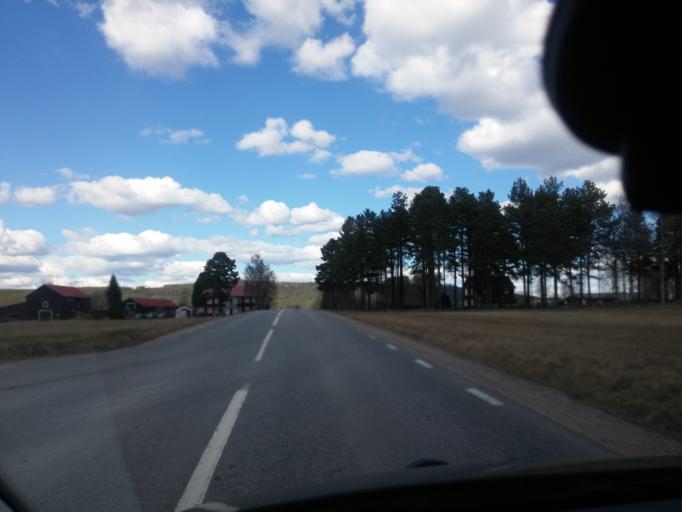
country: SE
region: Gaevleborg
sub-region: Ljusdals Kommun
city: Farila
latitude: 61.7903
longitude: 15.8305
